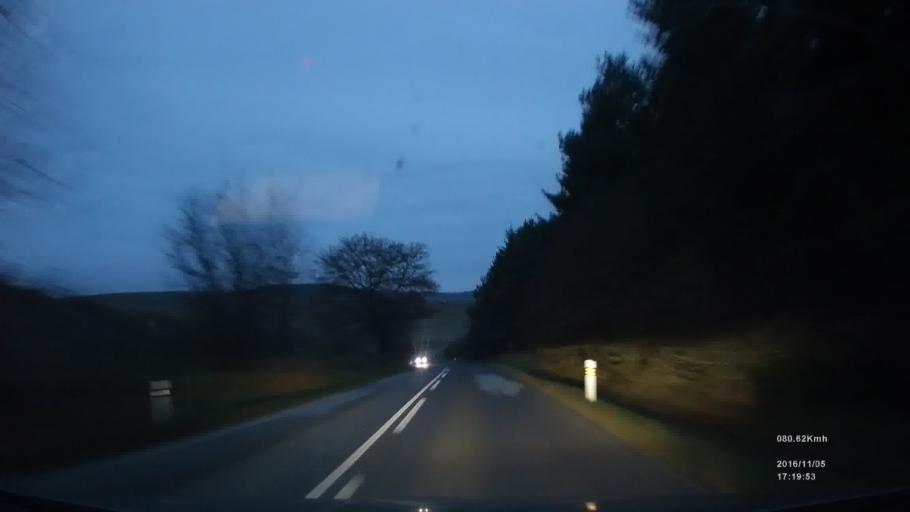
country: SK
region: Presovsky
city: Lubica
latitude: 49.0770
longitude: 20.4315
